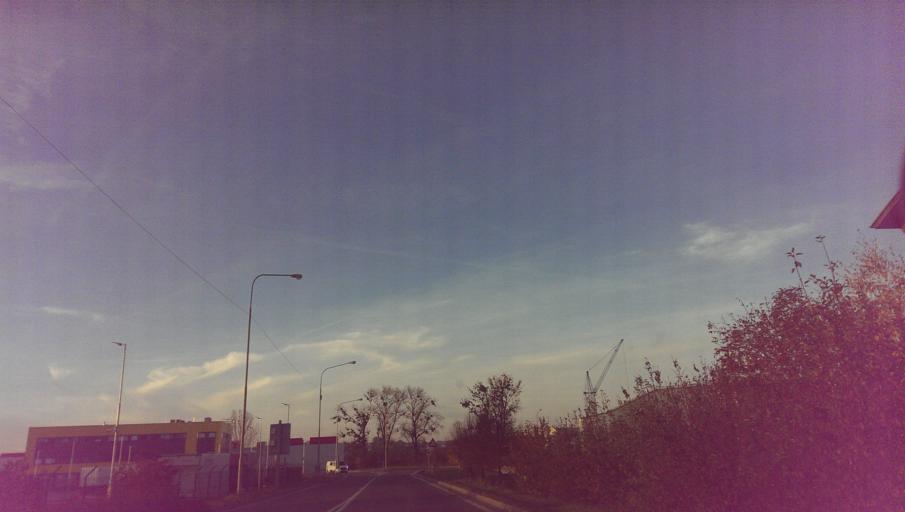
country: CZ
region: Zlin
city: Tecovice
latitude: 49.2104
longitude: 17.5909
